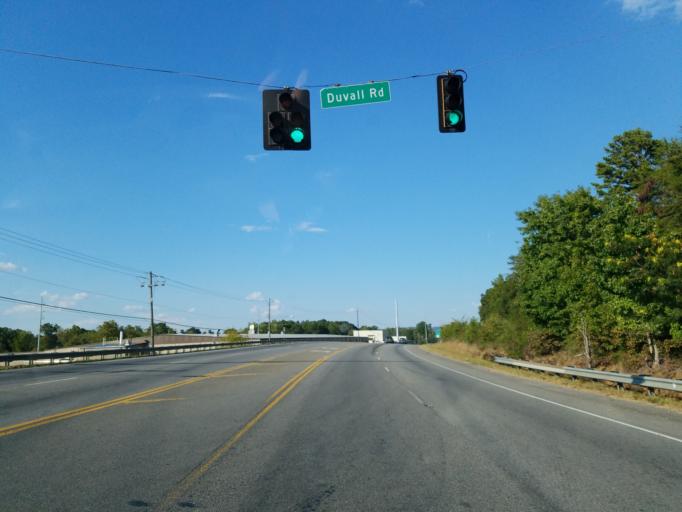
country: US
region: Georgia
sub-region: Murray County
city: Chatsworth
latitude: 34.8004
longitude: -84.7725
